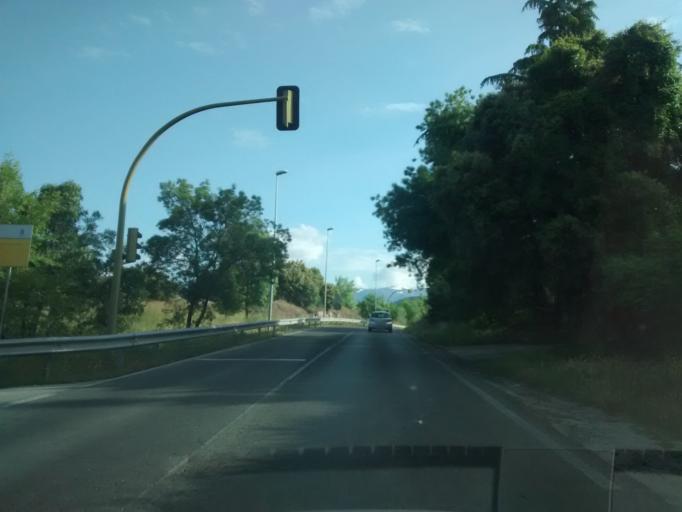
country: ES
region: Madrid
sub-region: Provincia de Madrid
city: Alpedrete
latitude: 40.6487
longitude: -4.0219
